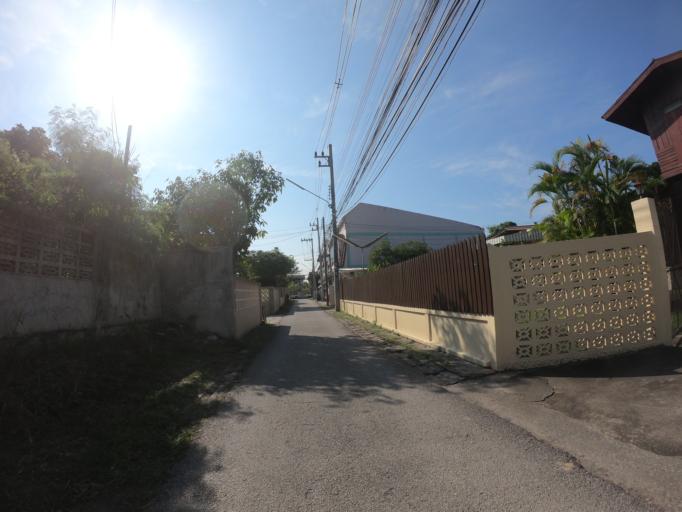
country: TH
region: Chiang Mai
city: Chiang Mai
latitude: 18.7941
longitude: 99.0160
